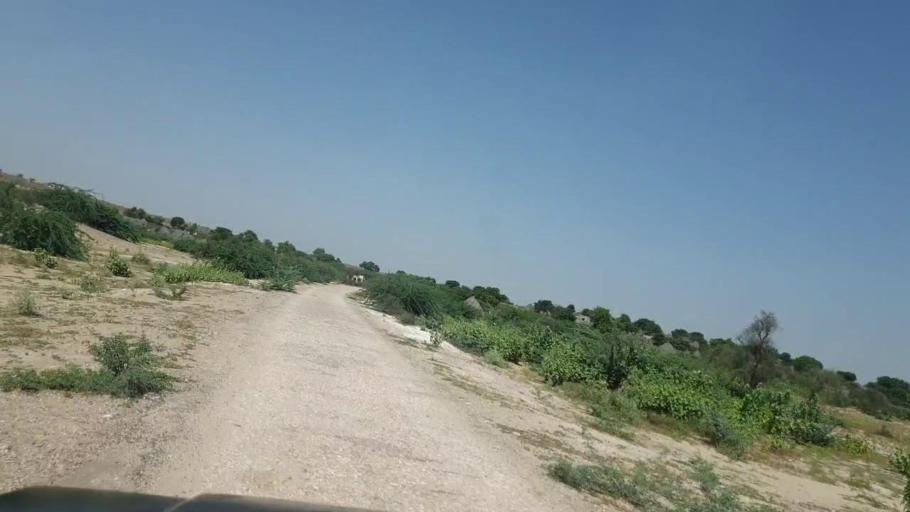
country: PK
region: Sindh
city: Chor
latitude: 25.3746
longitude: 70.3160
